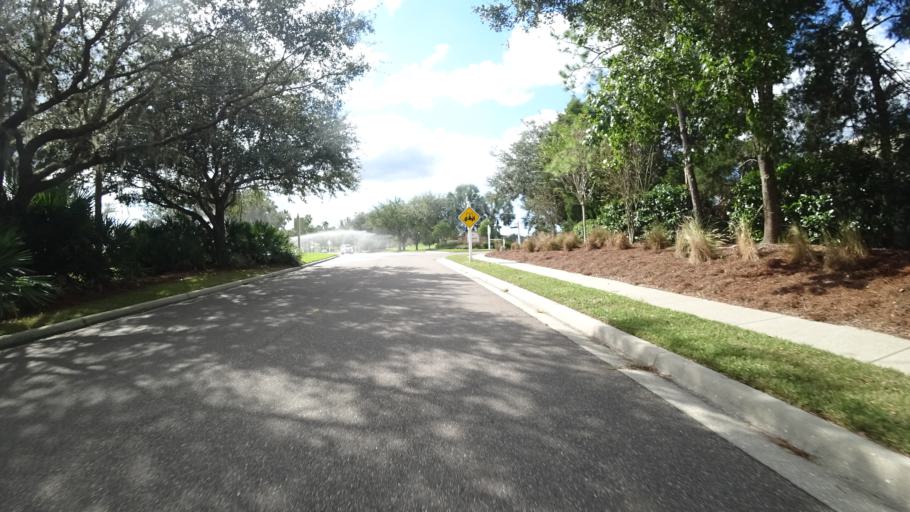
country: US
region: Florida
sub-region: Sarasota County
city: The Meadows
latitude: 27.3991
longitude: -82.4166
